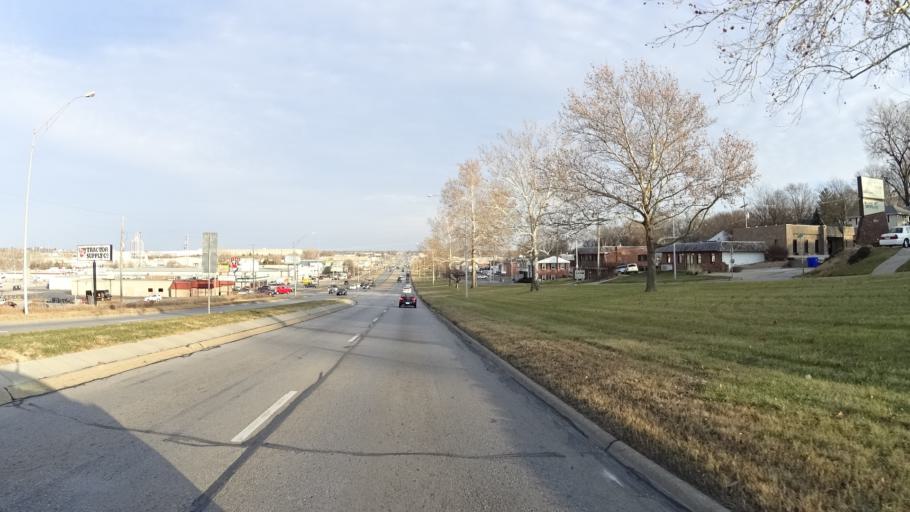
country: US
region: Nebraska
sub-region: Douglas County
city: Ralston
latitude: 41.2125
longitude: -96.0395
